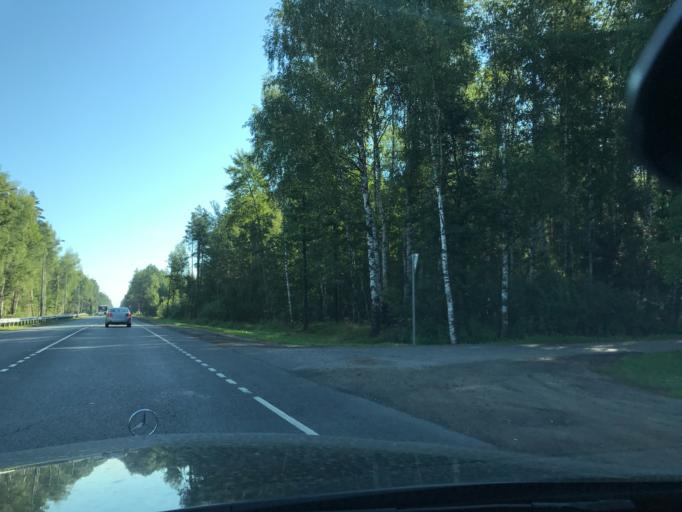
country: RU
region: Moskovskaya
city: Losino-Petrovskiy
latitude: 55.9425
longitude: 38.2221
